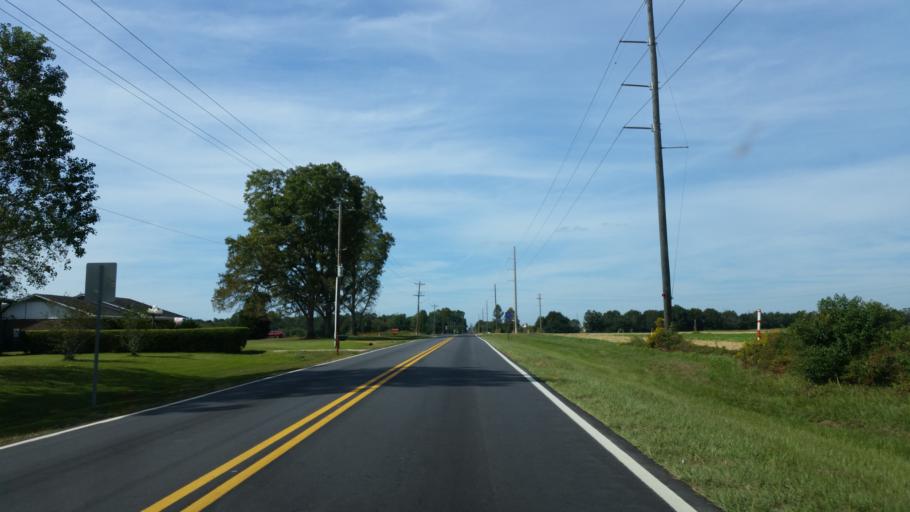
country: US
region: Alabama
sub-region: Baldwin County
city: Loxley
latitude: 30.6330
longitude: -87.7489
